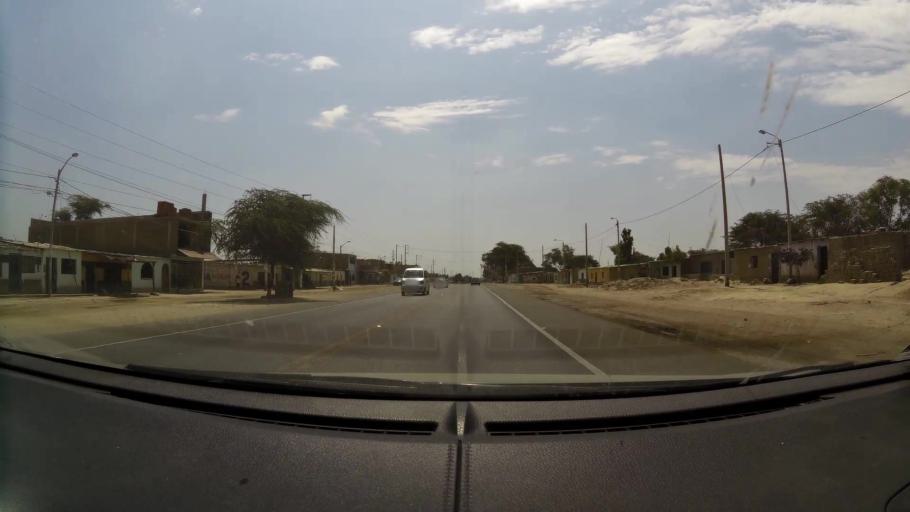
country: PE
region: La Libertad
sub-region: Chepen
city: Chepen
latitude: -7.1748
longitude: -79.4388
